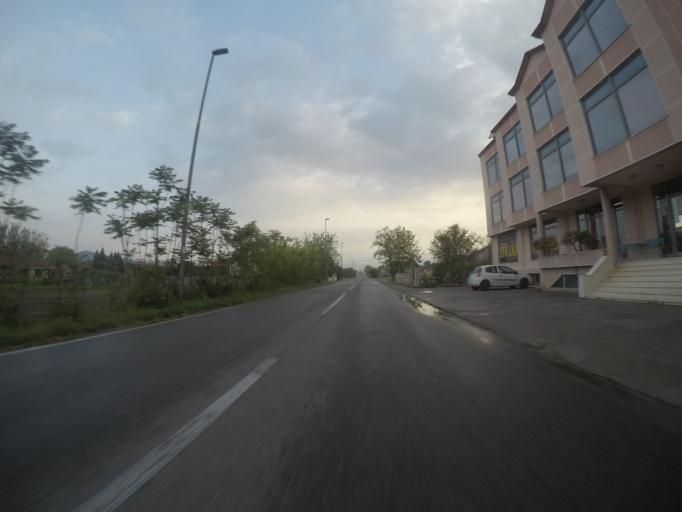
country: ME
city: Mojanovici
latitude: 42.3409
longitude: 19.2215
